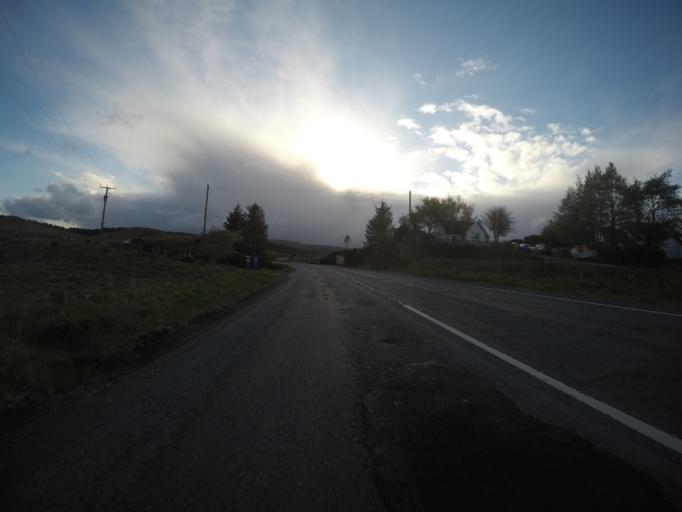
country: GB
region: Scotland
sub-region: Highland
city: Isle of Skye
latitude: 57.4535
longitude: -6.2962
